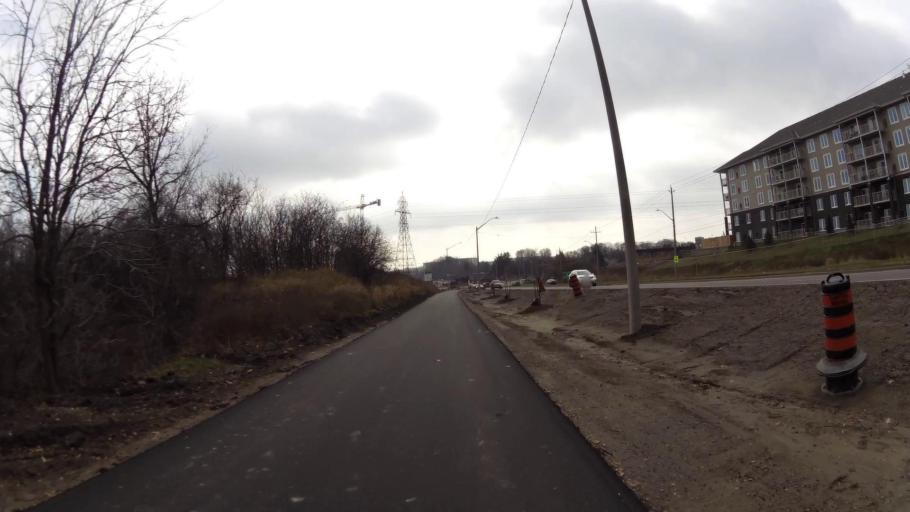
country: CA
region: Ontario
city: Kitchener
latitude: 43.4203
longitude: -80.4721
